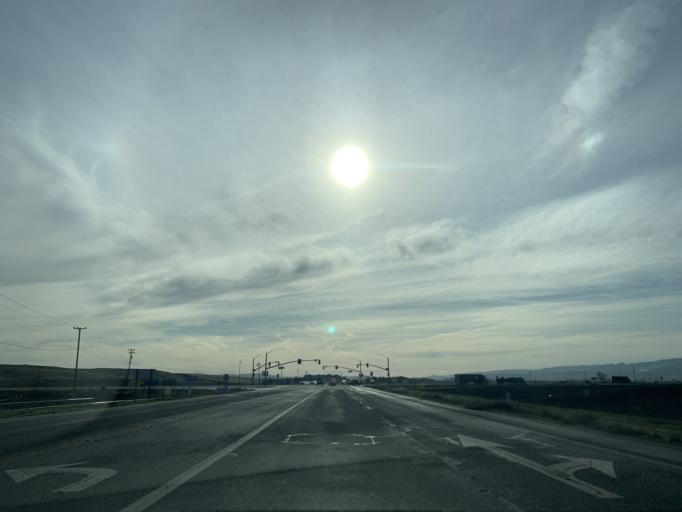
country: US
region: California
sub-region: San Benito County
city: Hollister
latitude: 36.8970
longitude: -121.4287
